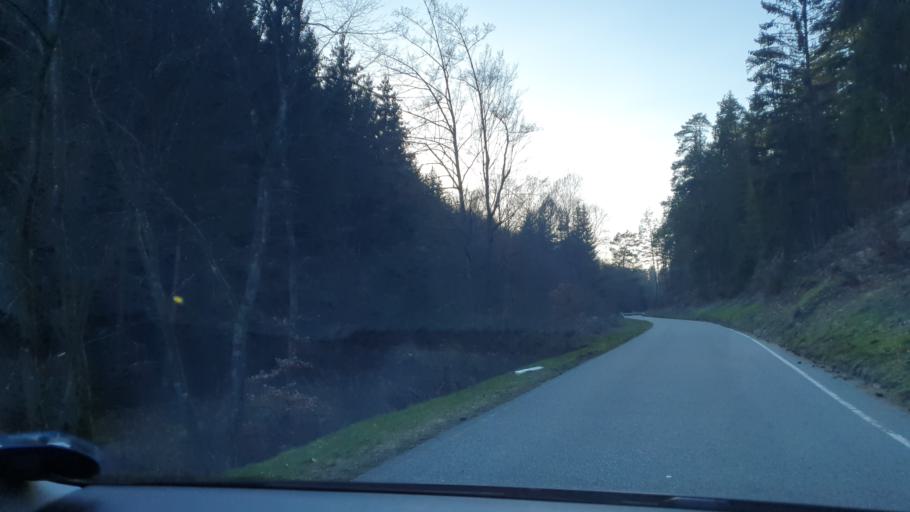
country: DE
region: Rheinland-Pfalz
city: Waldleiningen
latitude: 49.3953
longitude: 7.8642
